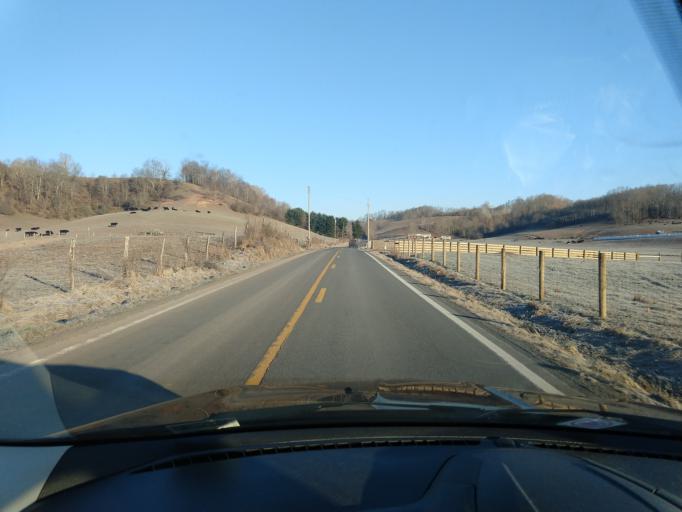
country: US
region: West Virginia
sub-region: Greenbrier County
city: Rainelle
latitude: 37.8640
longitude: -80.7197
